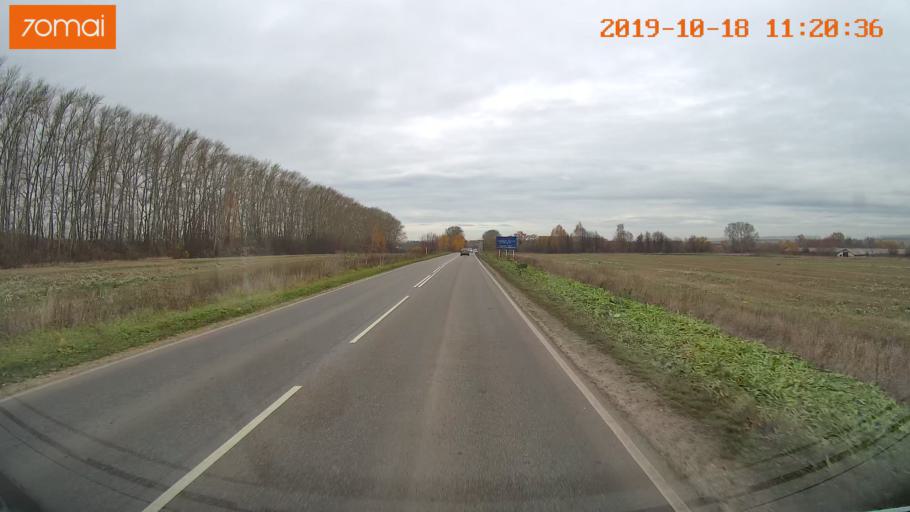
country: RU
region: Tula
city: Kimovsk
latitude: 54.0632
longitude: 38.5594
